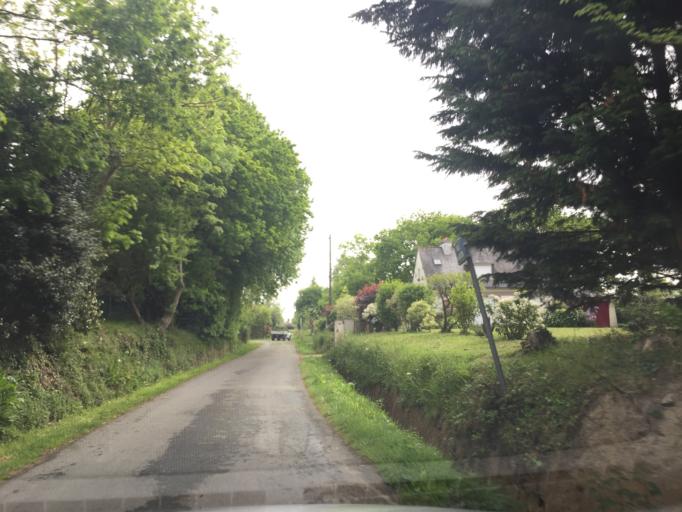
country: FR
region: Brittany
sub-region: Departement des Cotes-d'Armor
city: Saint-Cast-le-Guildo
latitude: 48.6000
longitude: -2.2331
